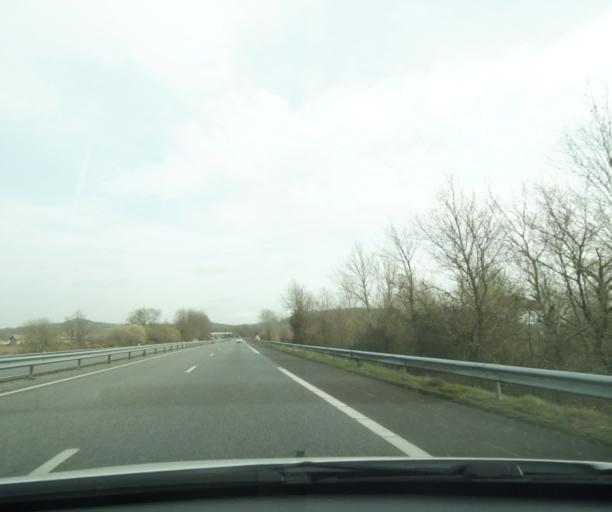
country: FR
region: Aquitaine
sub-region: Departement des Landes
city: Labatut
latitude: 43.5076
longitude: -1.0263
